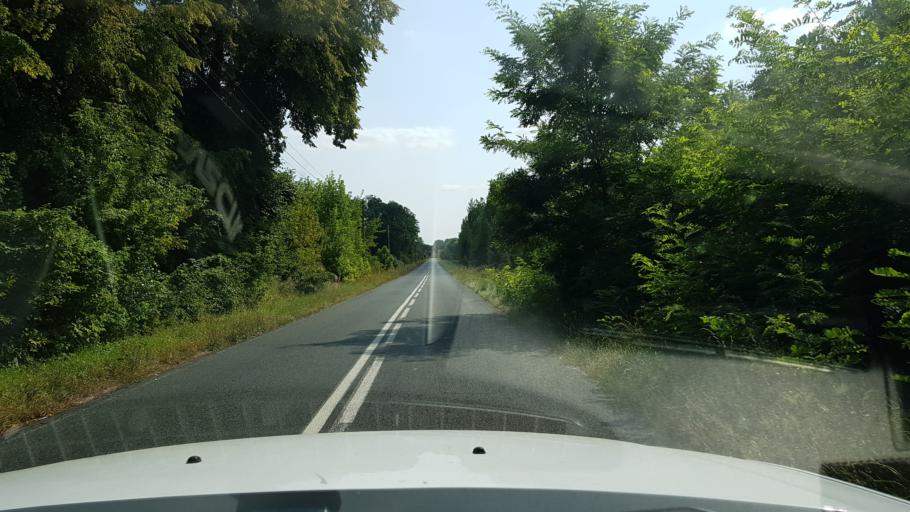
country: PL
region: West Pomeranian Voivodeship
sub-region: Powiat gryfinski
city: Cedynia
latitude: 52.8153
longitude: 14.2385
